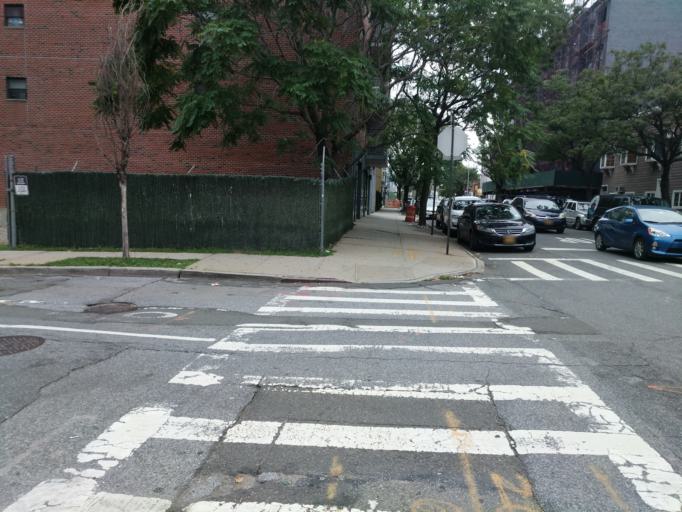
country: US
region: New York
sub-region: Queens County
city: Long Island City
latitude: 40.7513
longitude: -73.9376
